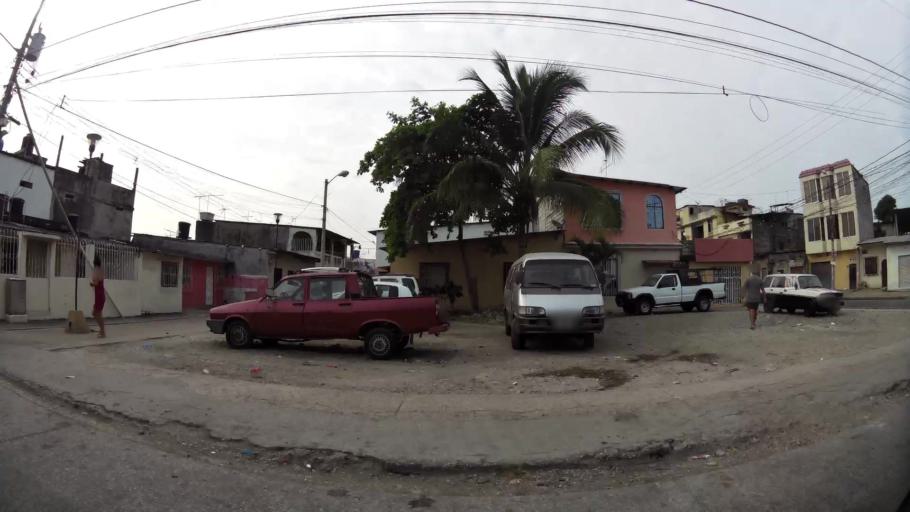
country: EC
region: Guayas
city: Guayaquil
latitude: -2.2547
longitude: -79.8882
